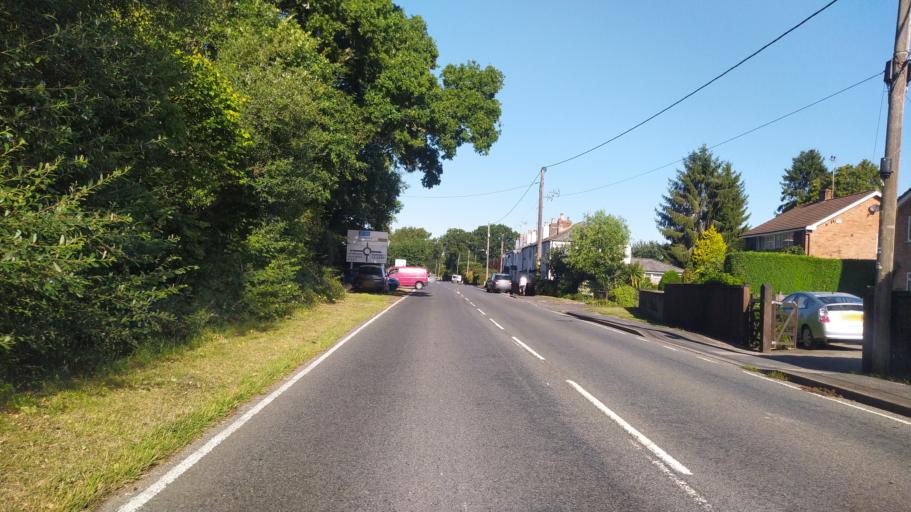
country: GB
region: England
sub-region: Hampshire
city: Cadnam
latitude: 50.9196
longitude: -1.5757
